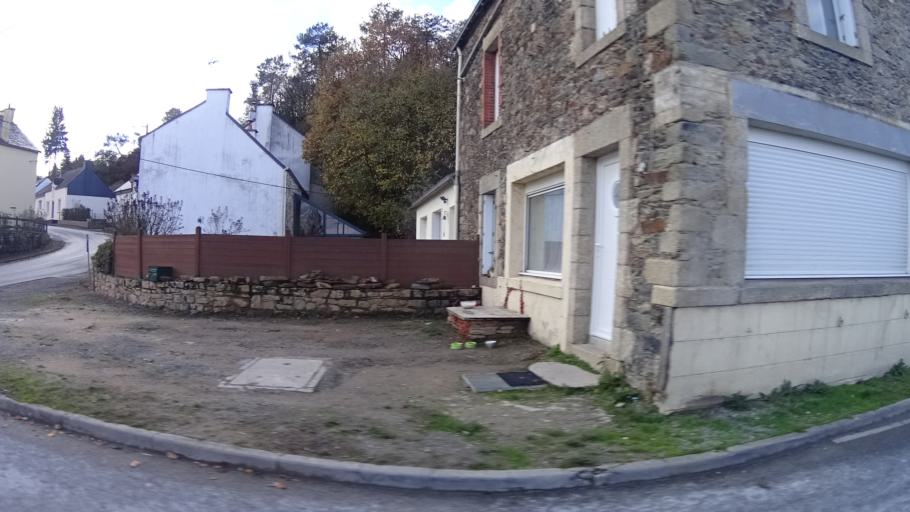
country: FR
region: Brittany
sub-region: Departement du Morbihan
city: Saint-Jean-la-Poterie
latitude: 47.6348
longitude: -2.1036
